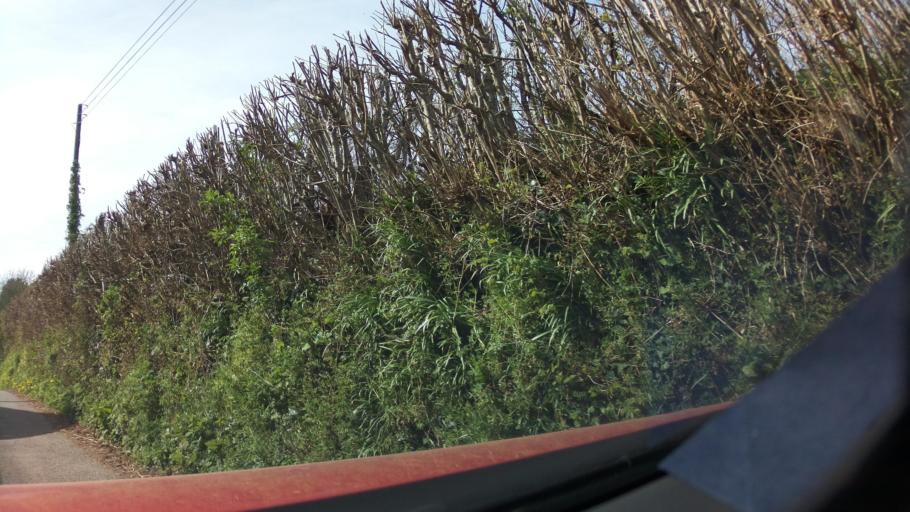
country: GB
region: England
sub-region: Dorset
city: Sherborne
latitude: 50.9803
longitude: -2.5322
